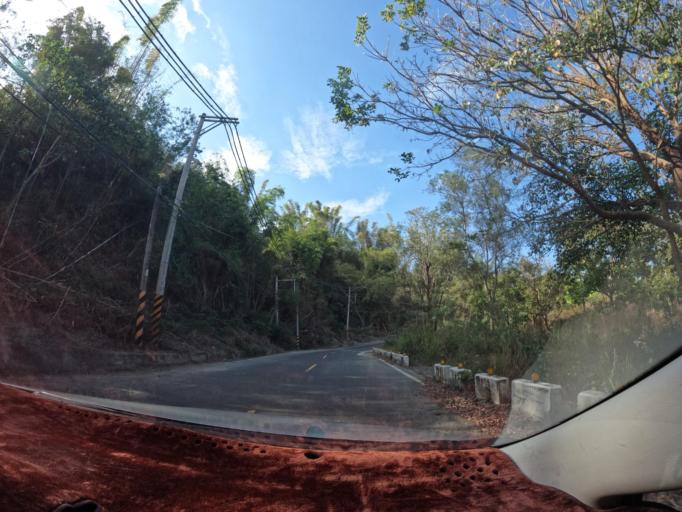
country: TW
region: Taiwan
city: Yujing
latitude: 23.0171
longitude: 120.3978
